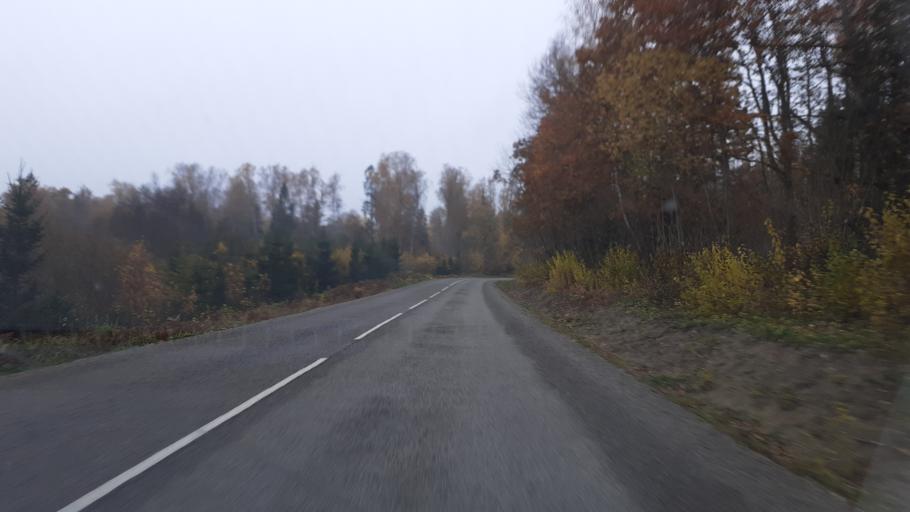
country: LV
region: Kuldigas Rajons
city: Kuldiga
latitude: 56.9527
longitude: 21.8709
